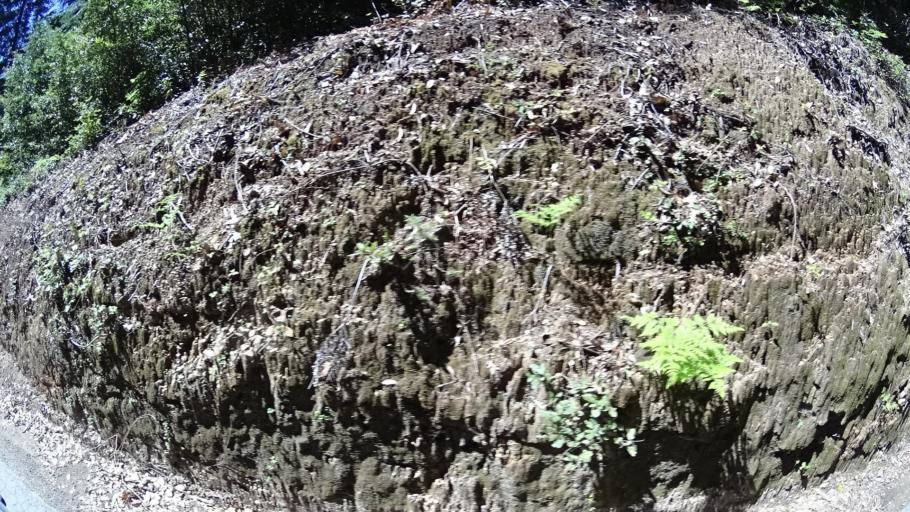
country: US
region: California
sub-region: Humboldt County
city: Redway
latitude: 40.0936
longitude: -123.9505
